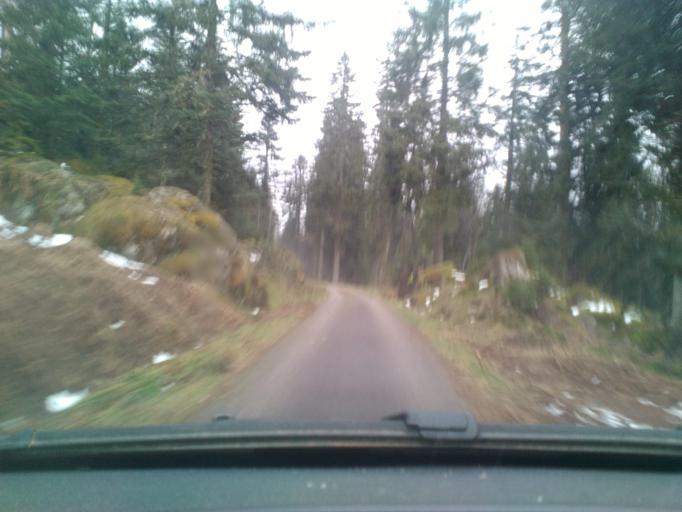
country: FR
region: Lorraine
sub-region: Departement des Vosges
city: Gerardmer
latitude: 48.1079
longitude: 6.8733
